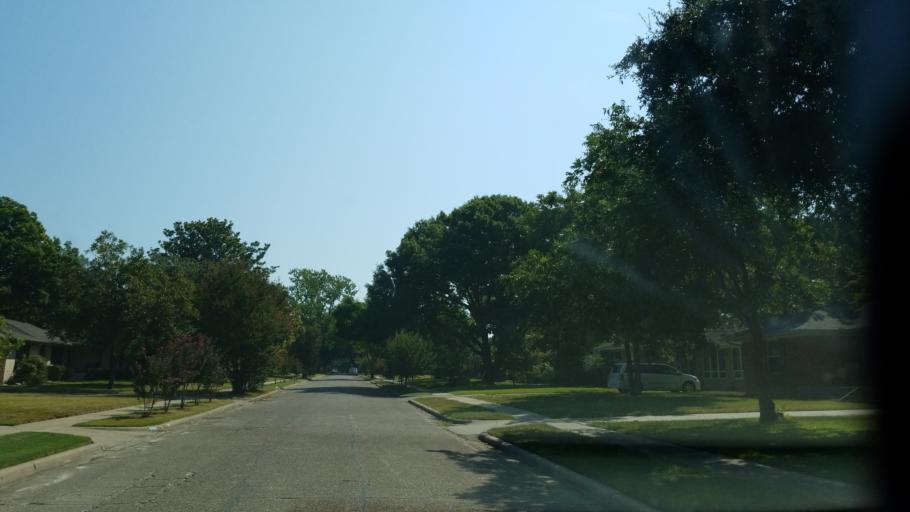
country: US
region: Texas
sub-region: Dallas County
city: Richardson
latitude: 32.9564
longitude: -96.7435
